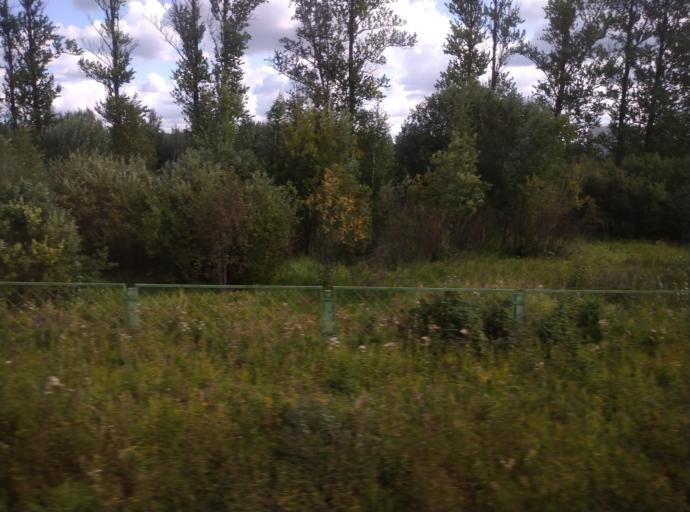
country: RU
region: St.-Petersburg
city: Kolpino
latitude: 59.7407
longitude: 30.6257
